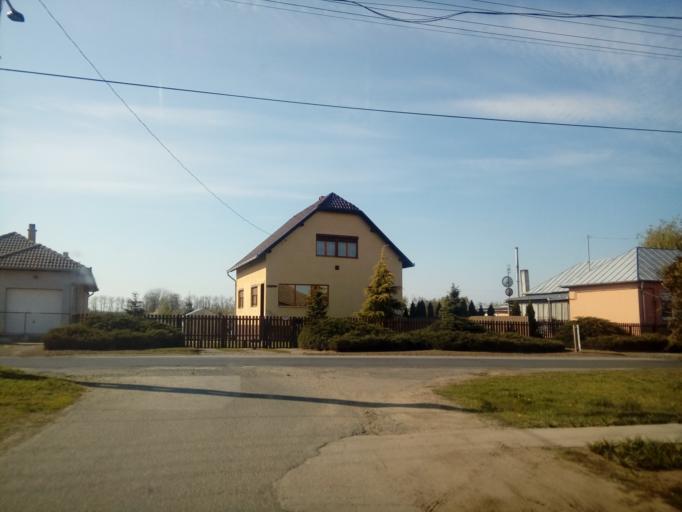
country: HU
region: Szabolcs-Szatmar-Bereg
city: Balkany
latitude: 47.7705
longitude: 21.8468
